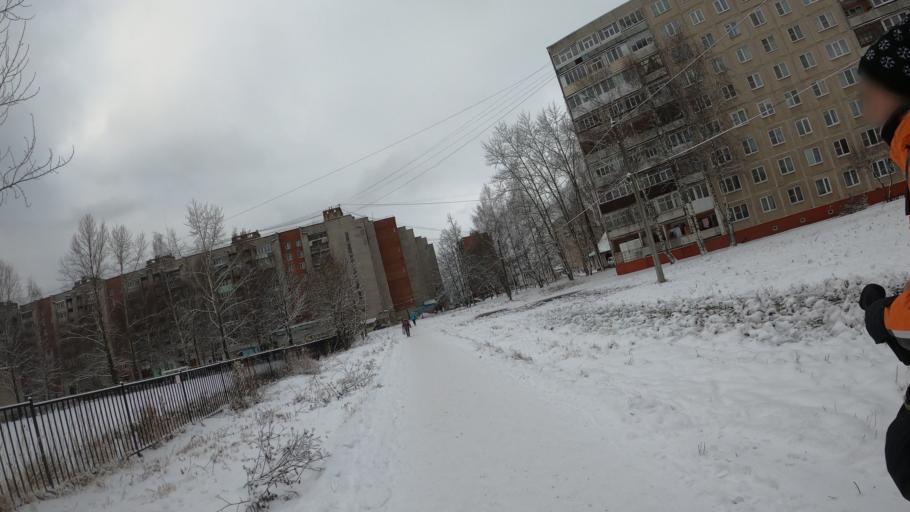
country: RU
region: Jaroslavl
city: Pereslavl'-Zalesskiy
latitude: 56.7507
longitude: 38.8777
